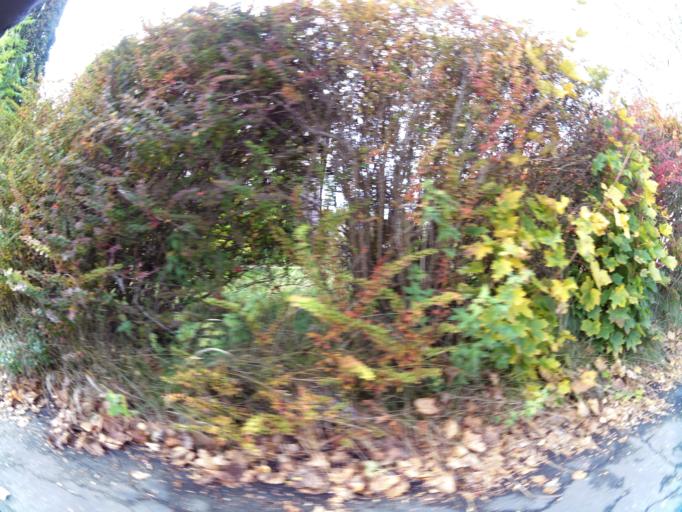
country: NO
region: Ostfold
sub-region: Fredrikstad
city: Fredrikstad
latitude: 59.2177
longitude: 10.9305
